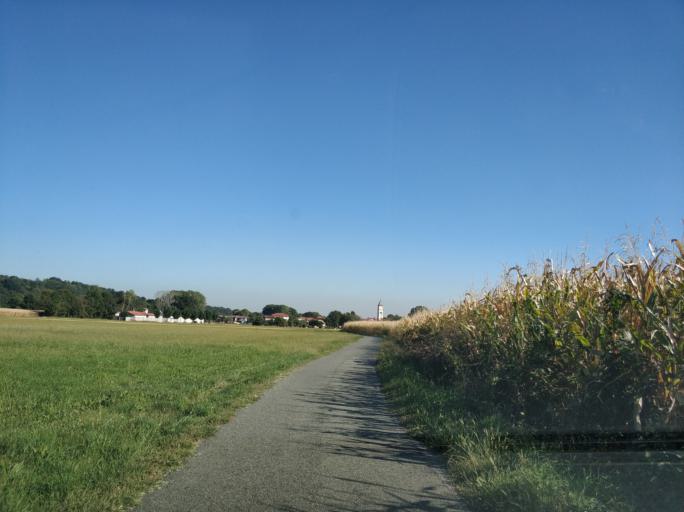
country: IT
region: Piedmont
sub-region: Provincia di Torino
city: Grosso
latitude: 45.2605
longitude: 7.5524
